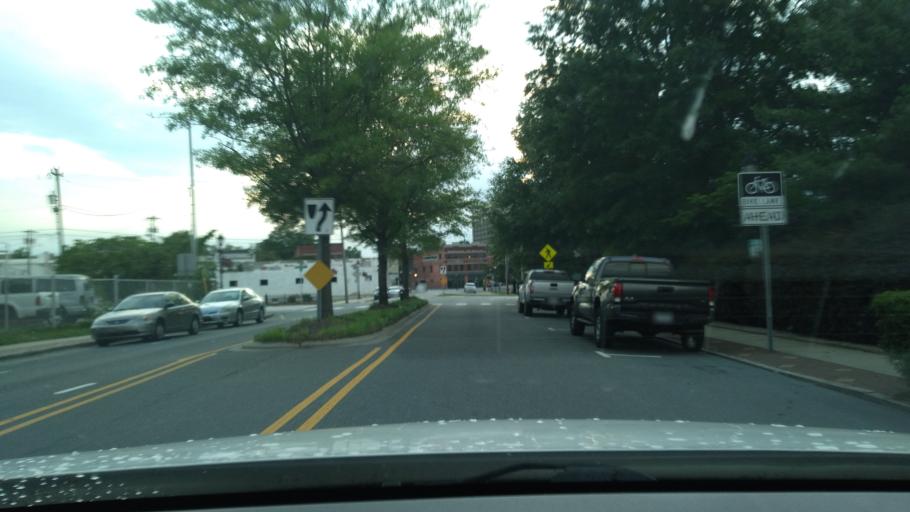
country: US
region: North Carolina
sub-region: Guilford County
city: Greensboro
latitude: 36.0668
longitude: -79.7886
